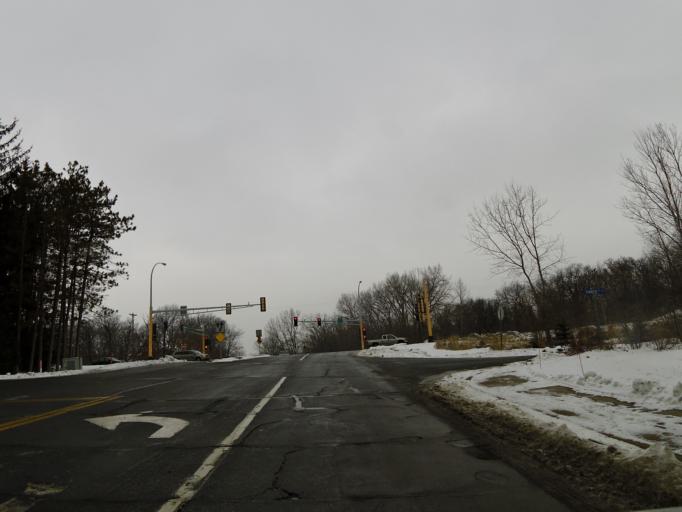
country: US
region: Minnesota
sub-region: Scott County
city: Prior Lake
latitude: 44.7252
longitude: -93.4031
